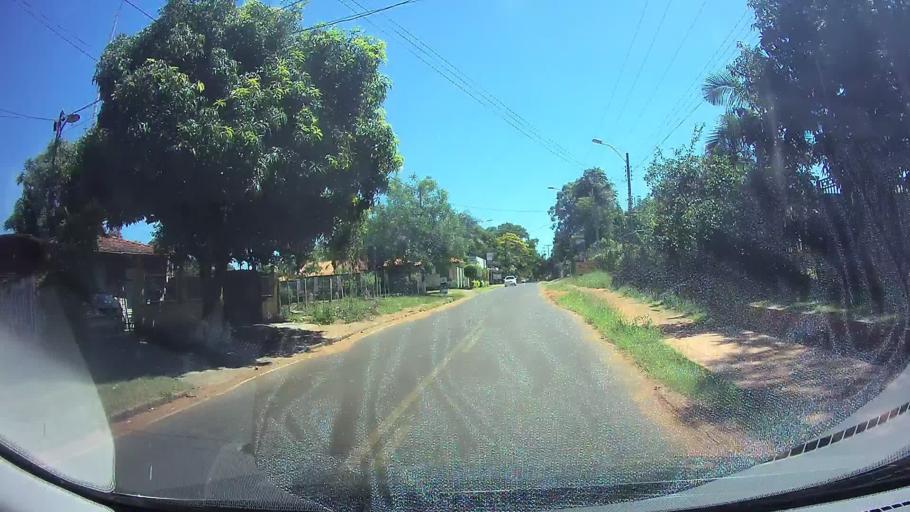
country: PY
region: Central
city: Aregua
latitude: -25.2924
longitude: -57.4118
